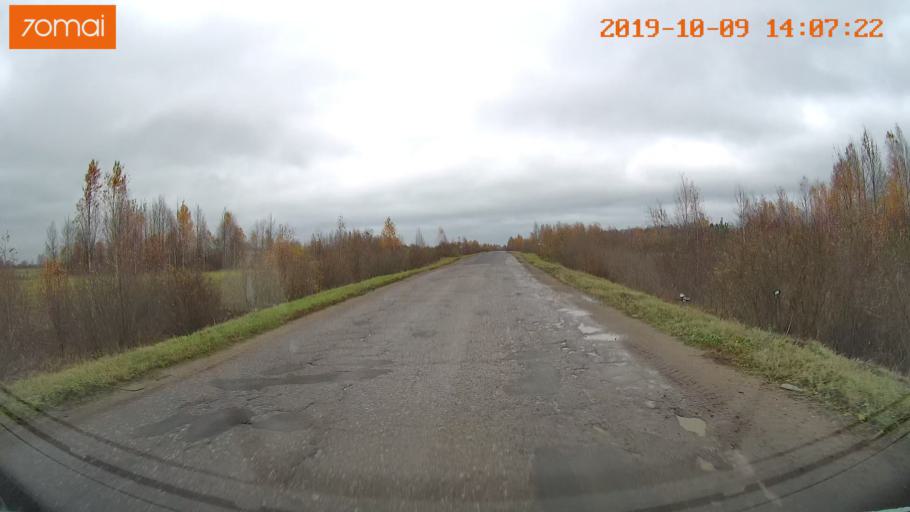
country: RU
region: Kostroma
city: Buy
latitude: 58.4701
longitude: 41.4217
